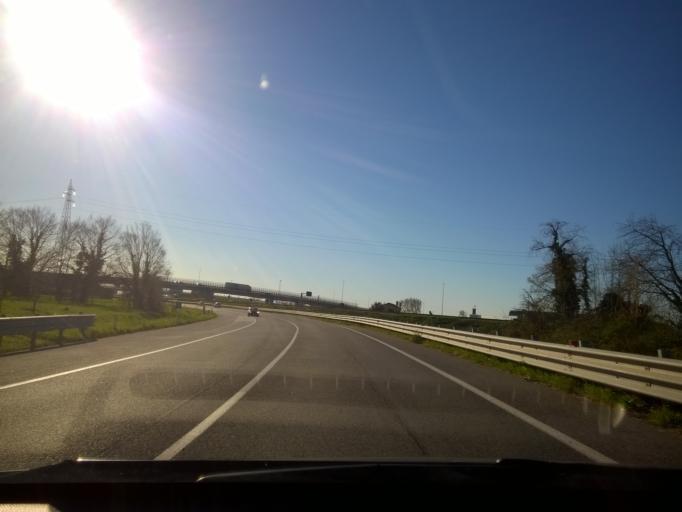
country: IT
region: Veneto
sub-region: Provincia di Venezia
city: San Liberale
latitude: 45.5743
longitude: 12.3464
